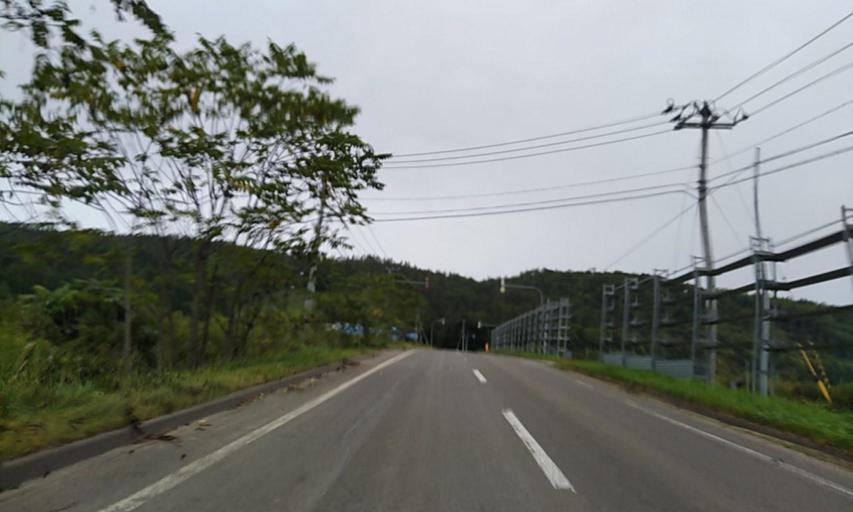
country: JP
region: Hokkaido
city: Bihoro
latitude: 43.6253
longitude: 144.1055
